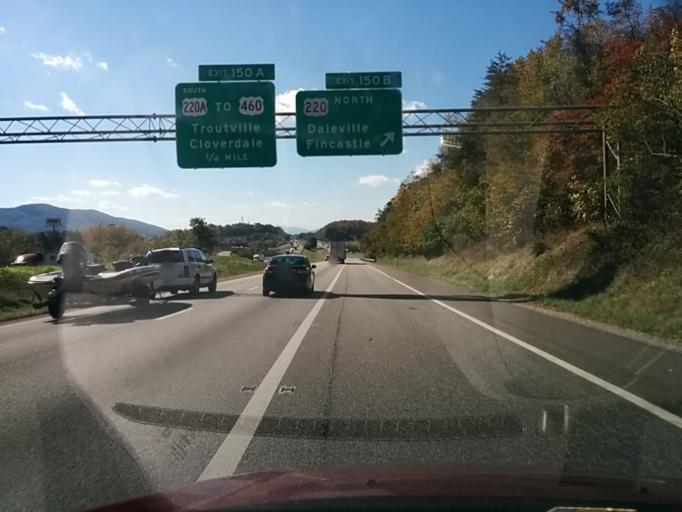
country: US
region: Virginia
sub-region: Botetourt County
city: Daleville
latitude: 37.3953
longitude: -79.9015
